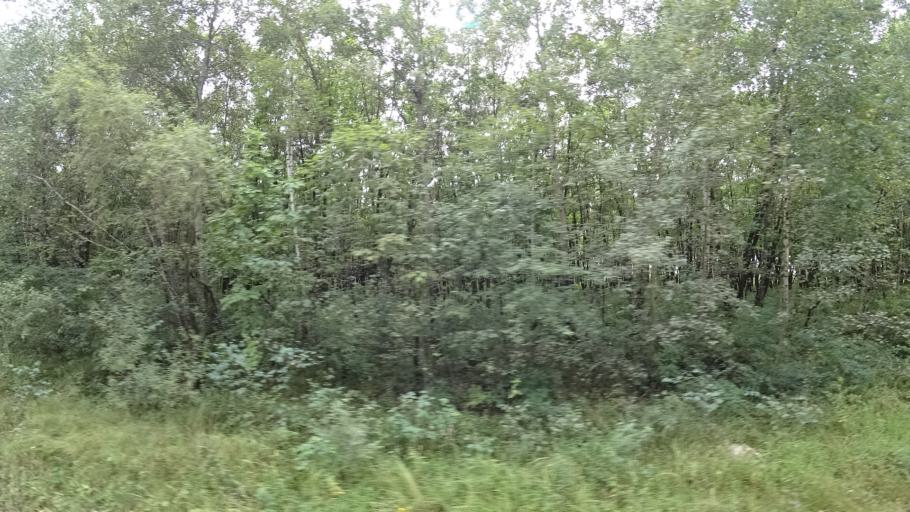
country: RU
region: Primorskiy
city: Lyalichi
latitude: 44.0869
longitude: 132.4383
